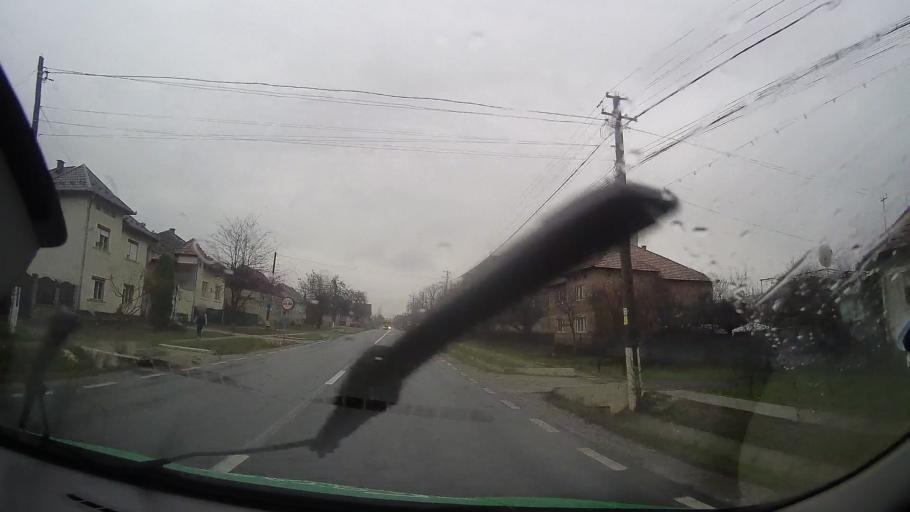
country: RO
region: Bistrita-Nasaud
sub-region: Comuna Galatii Bistritei
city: Galatii Bistritei
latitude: 46.9709
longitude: 24.4334
